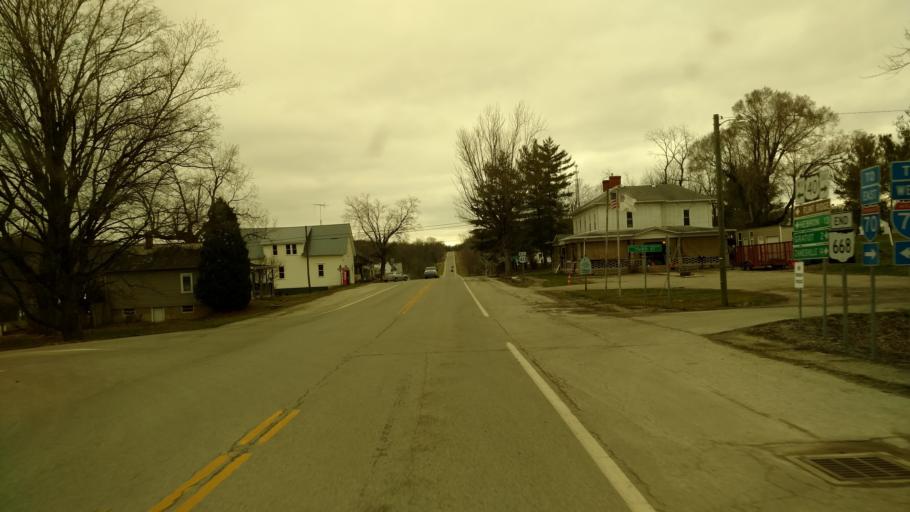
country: US
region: Ohio
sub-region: Perry County
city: Somerset
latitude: 39.9469
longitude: -82.2560
